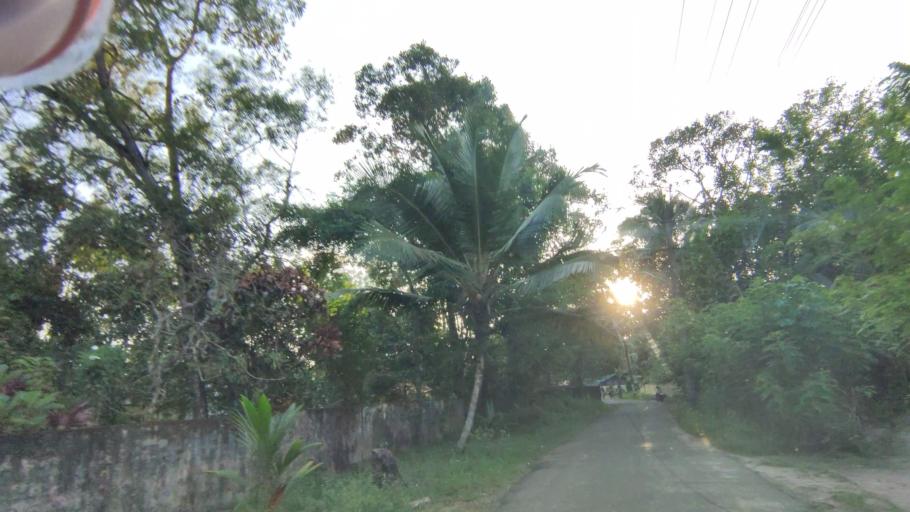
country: IN
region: Kerala
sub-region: Alappuzha
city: Shertallai
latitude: 9.6475
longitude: 76.3412
